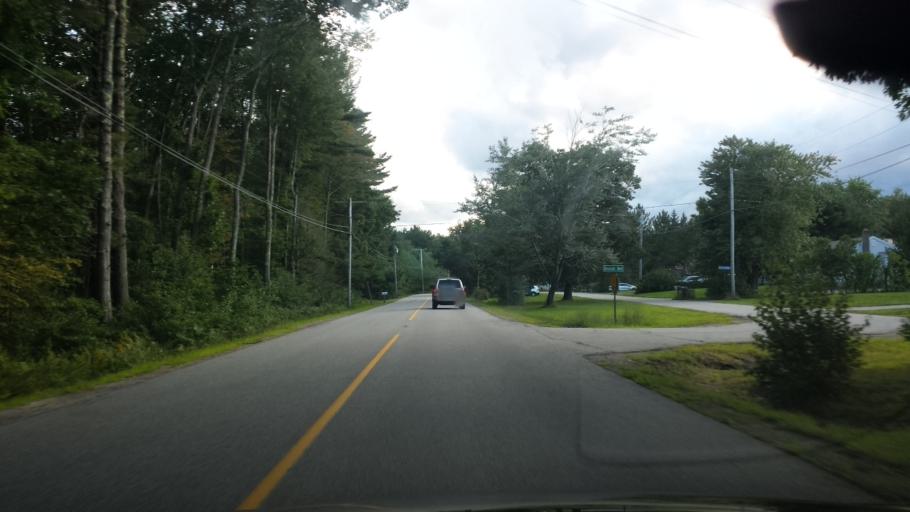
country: US
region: Maine
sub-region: York County
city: Arundel
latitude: 43.4343
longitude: -70.4513
